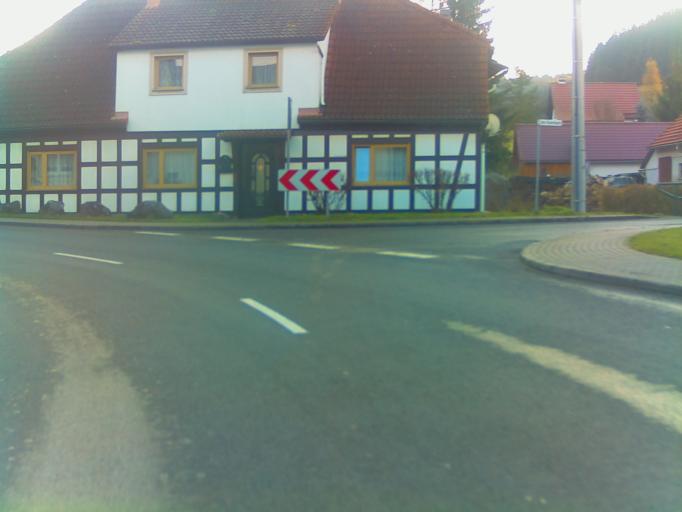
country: DE
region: Thuringia
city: Schleusingen
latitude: 50.4761
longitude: 10.8005
